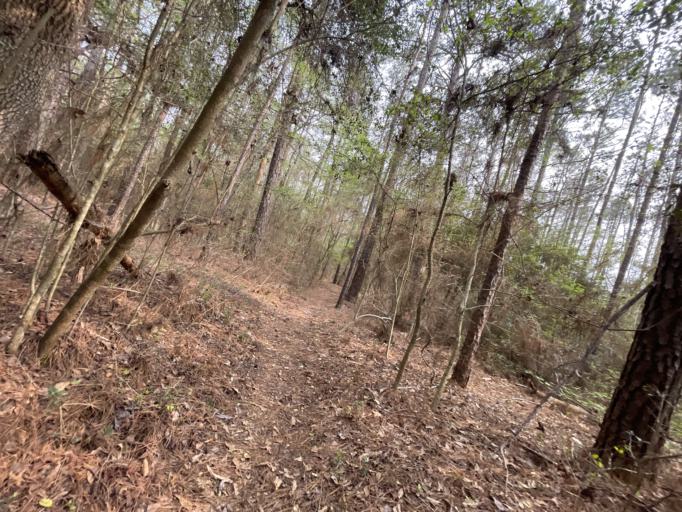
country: US
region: Texas
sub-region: Walker County
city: Huntsville
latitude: 30.6539
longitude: -95.4857
